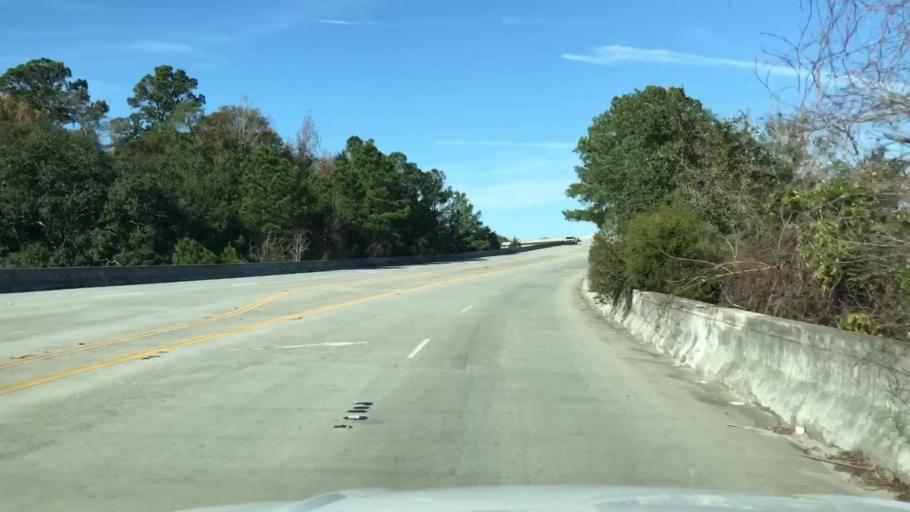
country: US
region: South Carolina
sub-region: Charleston County
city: Charleston
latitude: 32.7777
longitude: -79.9674
